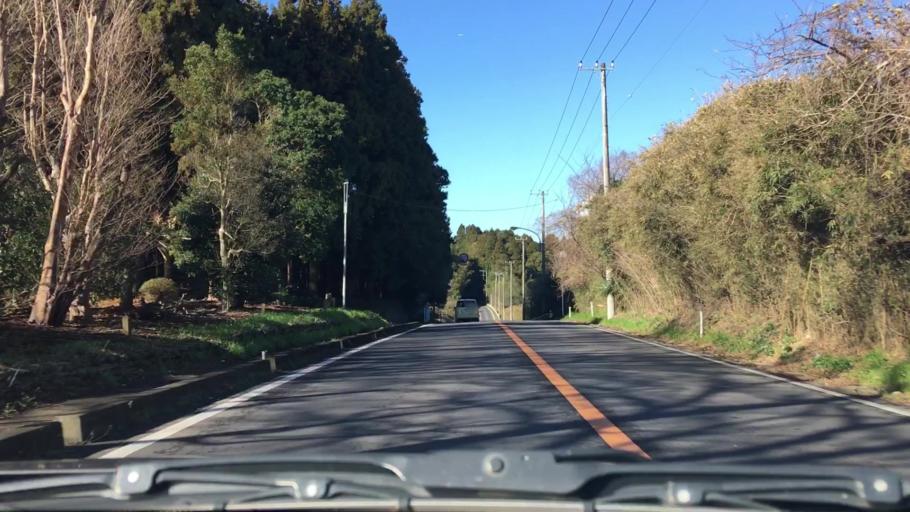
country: JP
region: Chiba
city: Sawara
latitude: 35.8164
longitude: 140.5126
